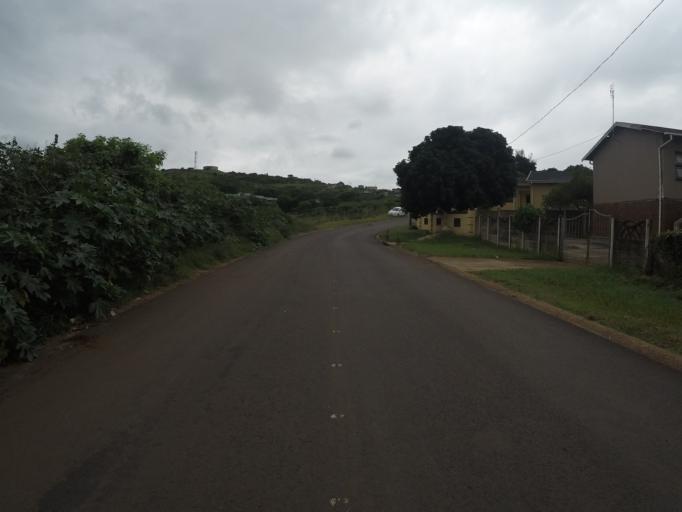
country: ZA
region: KwaZulu-Natal
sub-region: uThungulu District Municipality
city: Empangeni
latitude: -28.7732
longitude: 31.8605
